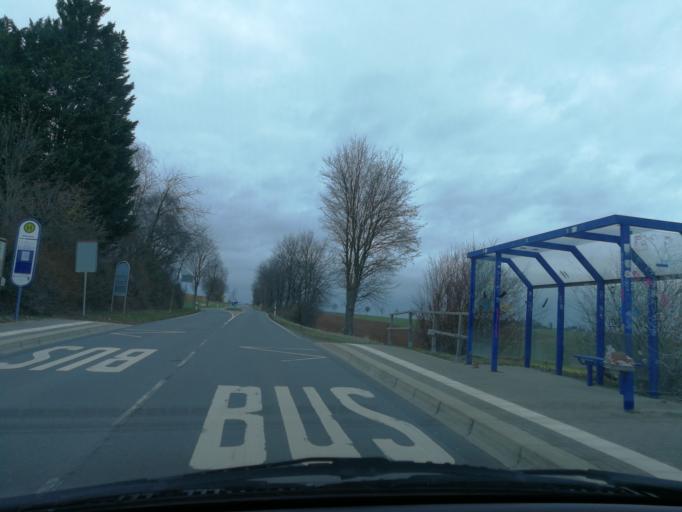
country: DE
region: Hesse
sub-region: Regierungsbezirk Darmstadt
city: Rossdorf
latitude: 49.8480
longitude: 8.7909
